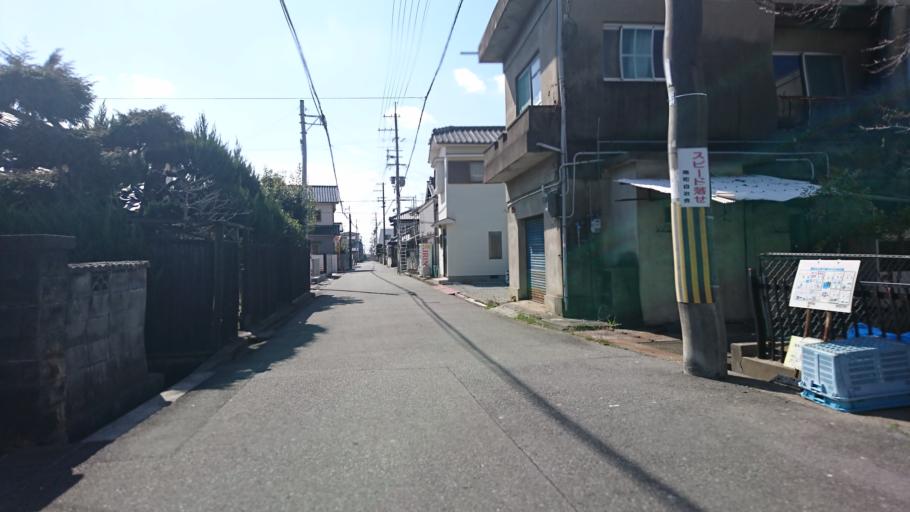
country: JP
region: Hyogo
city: Kakogawacho-honmachi
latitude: 34.8151
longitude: 134.8208
